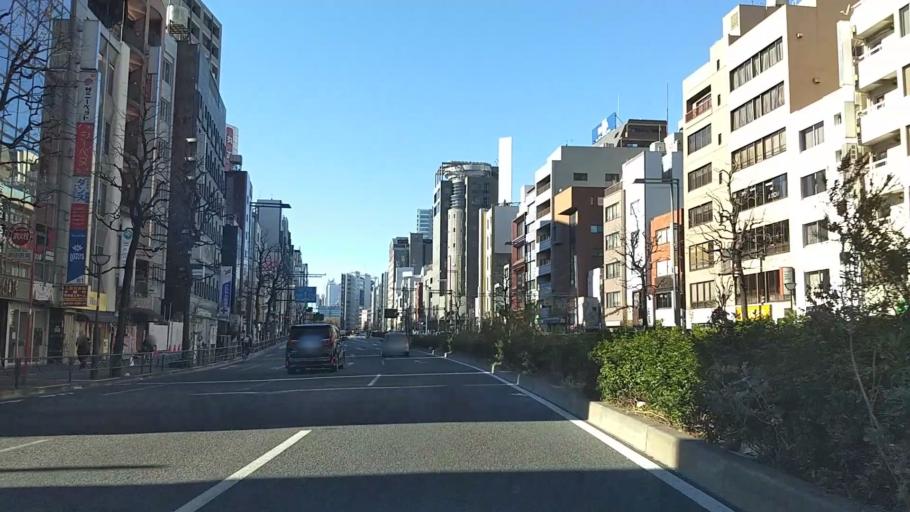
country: JP
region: Tokyo
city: Tokyo
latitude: 35.6881
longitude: 139.7222
